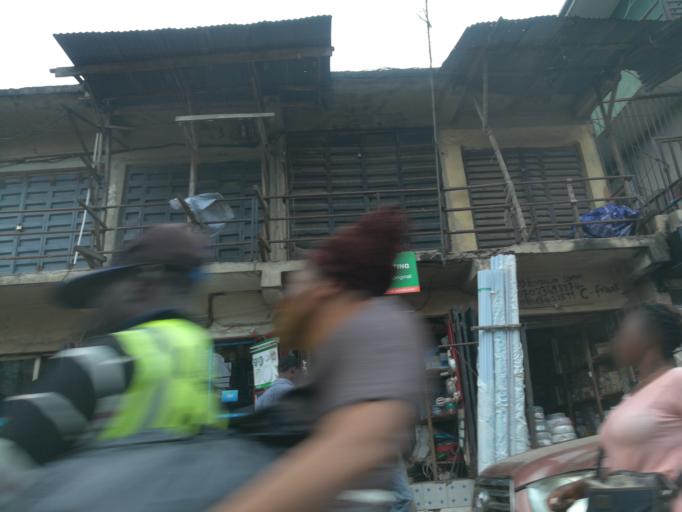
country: NG
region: Lagos
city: Oshodi
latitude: 6.5593
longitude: 3.3482
